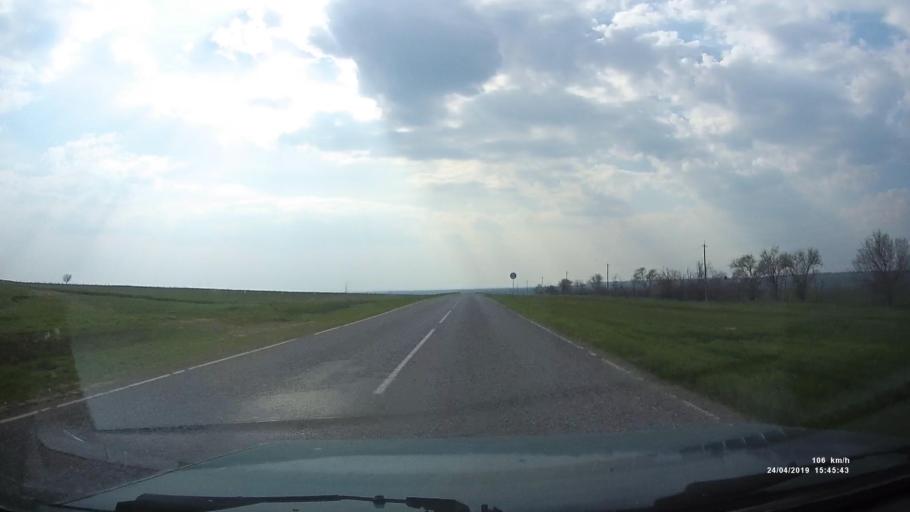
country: RU
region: Kalmykiya
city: Yashalta
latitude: 46.5918
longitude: 42.7310
